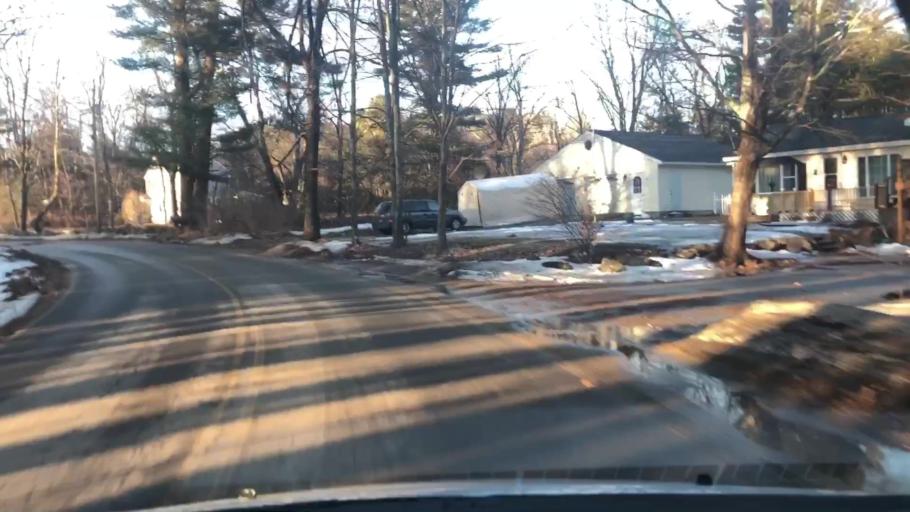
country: US
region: New Hampshire
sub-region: Hillsborough County
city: Milford
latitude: 42.8061
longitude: -71.6469
